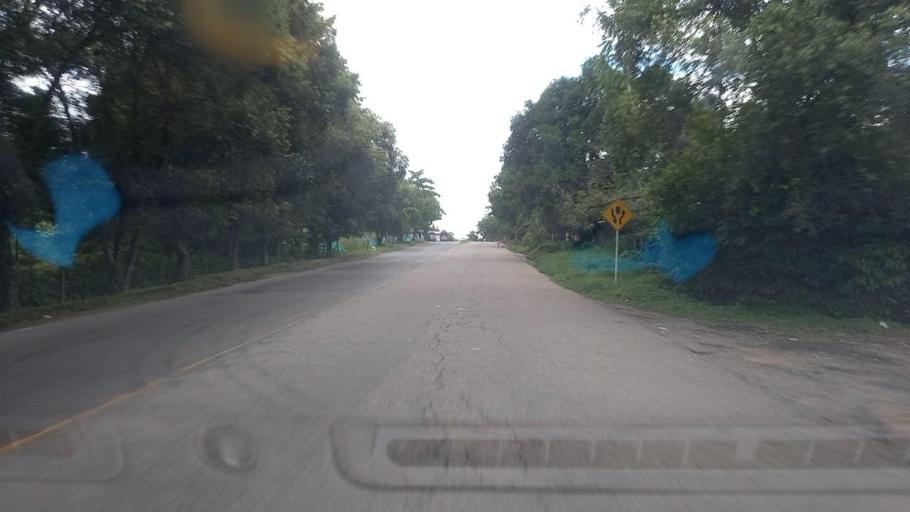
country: CO
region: Santander
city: Sabana de Torres
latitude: 7.1303
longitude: -73.5639
